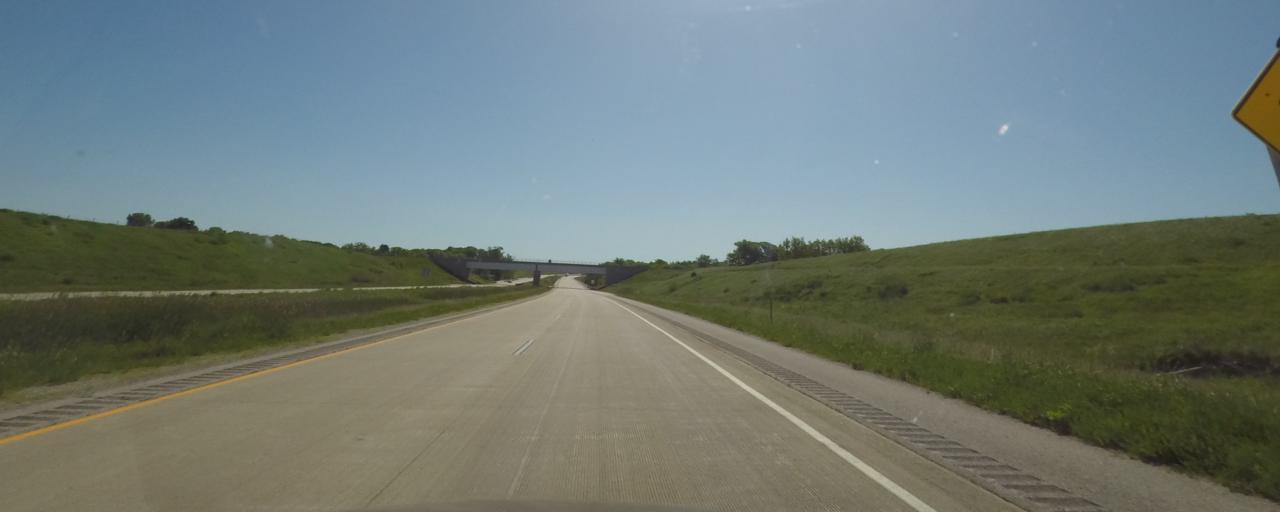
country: US
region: Wisconsin
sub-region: Fond du Lac County
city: Fond du Lac
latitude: 43.7362
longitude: -88.4648
